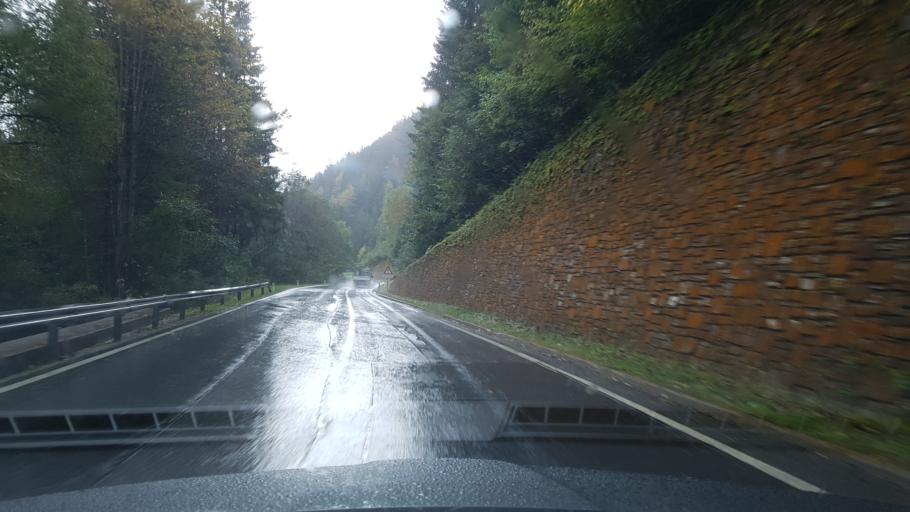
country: AT
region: Styria
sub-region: Politischer Bezirk Voitsberg
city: Salla
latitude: 47.1040
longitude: 14.9625
